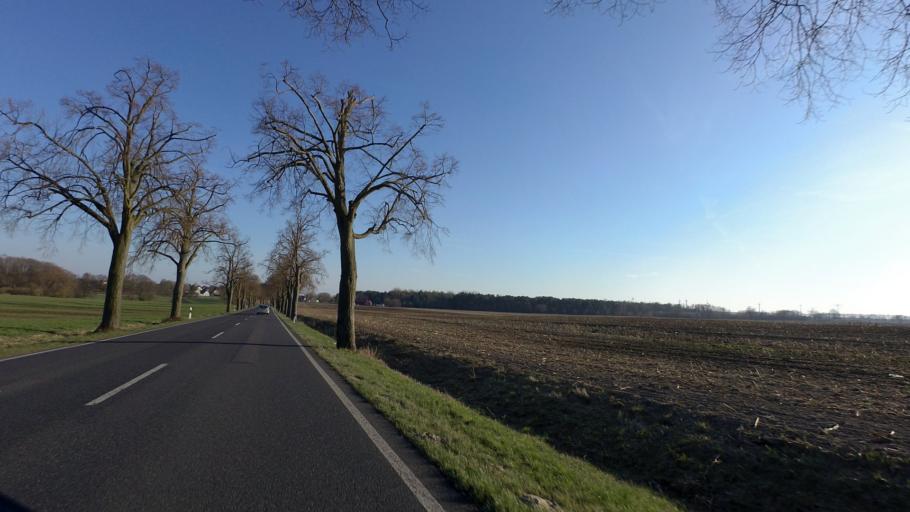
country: DE
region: Brandenburg
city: Britz
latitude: 52.8946
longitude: 13.8041
